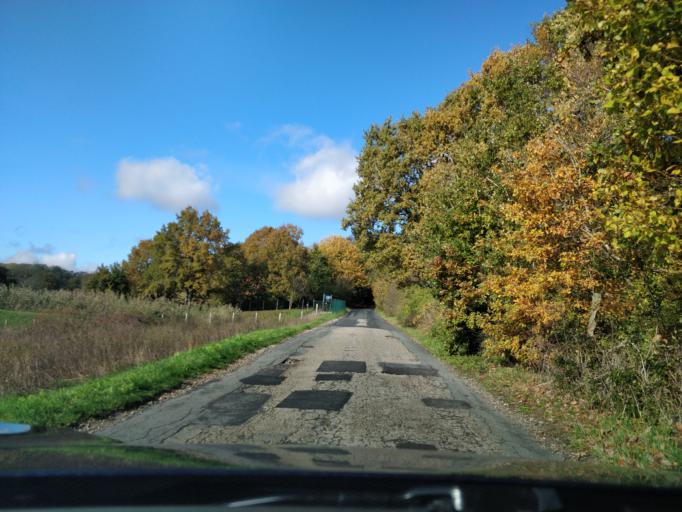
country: FR
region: Ile-de-France
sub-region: Departement de l'Essonne
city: Fontenay-les-Briis
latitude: 48.6303
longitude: 2.1614
